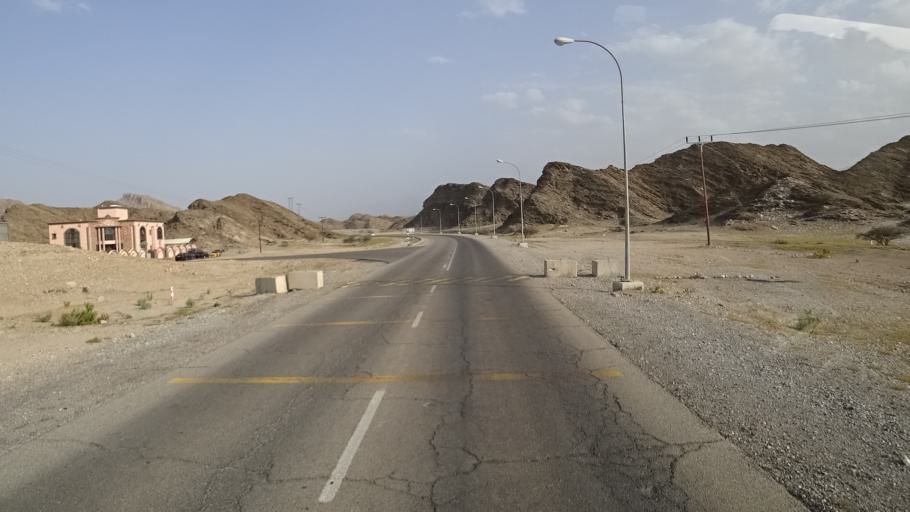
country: OM
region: Muhafazat Masqat
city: Bawshar
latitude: 23.3732
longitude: 58.5173
